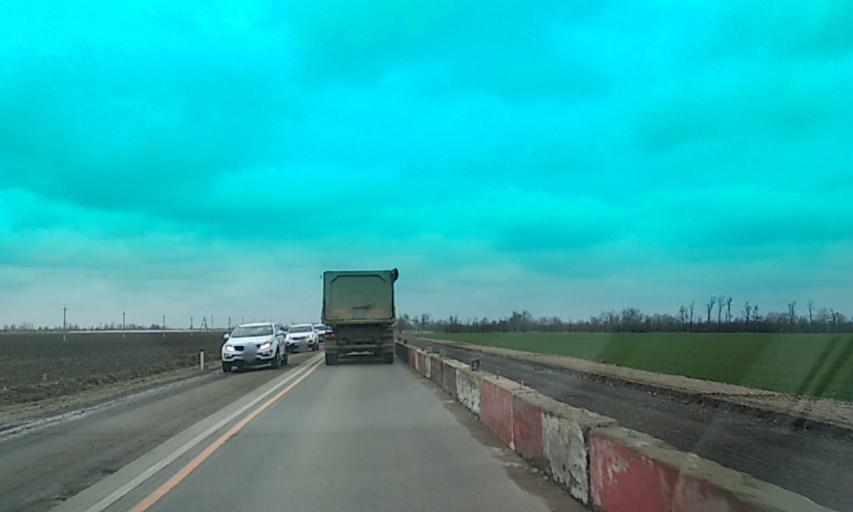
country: RU
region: Adygeya
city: Beloye
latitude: 45.0193
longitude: 39.6911
